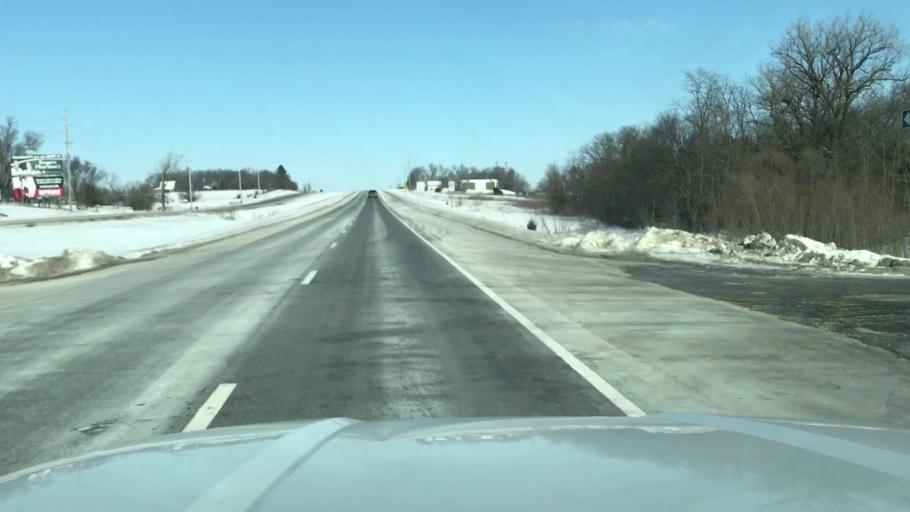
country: US
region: Missouri
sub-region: Nodaway County
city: Maryville
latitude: 40.2003
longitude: -94.8676
